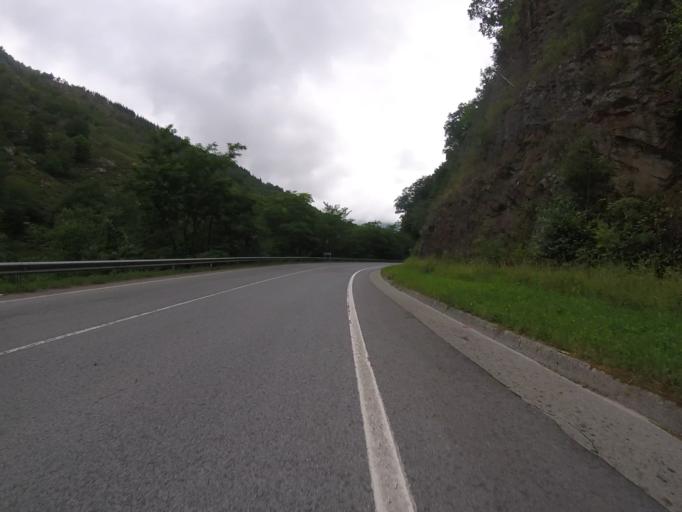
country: ES
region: Navarre
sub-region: Provincia de Navarra
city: Zubieta
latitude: 43.1108
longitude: -1.7634
